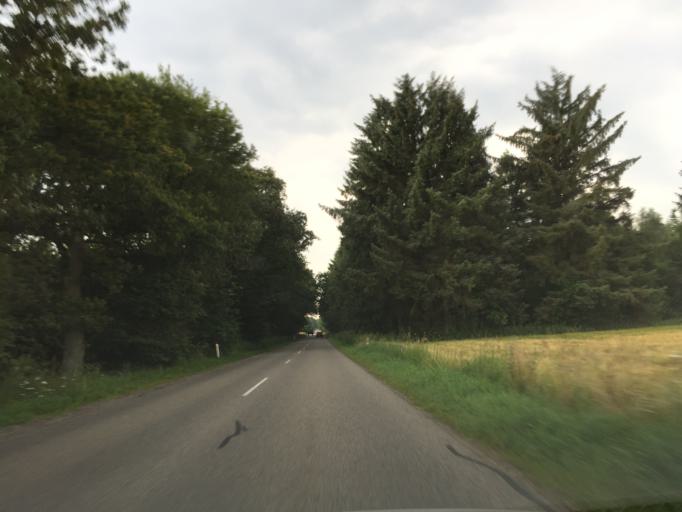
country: DK
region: Central Jutland
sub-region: Viborg Kommune
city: Bjerringbro
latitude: 56.3274
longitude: 9.6291
